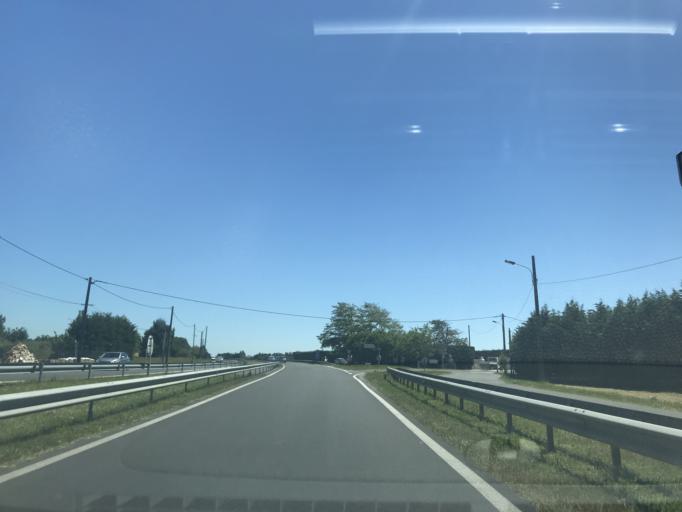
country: FR
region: Poitou-Charentes
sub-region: Departement de la Charente-Maritime
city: Vaux-sur-Mer
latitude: 45.6596
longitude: -1.0599
